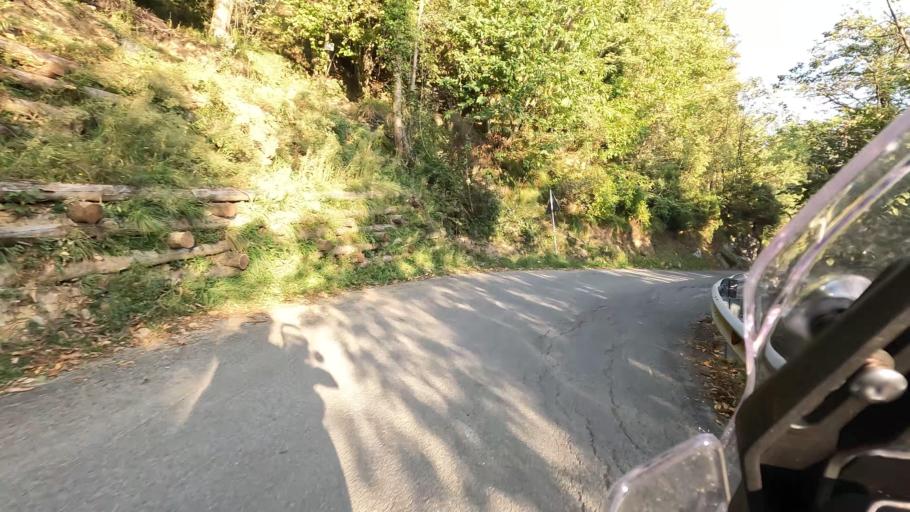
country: IT
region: Liguria
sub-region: Provincia di Savona
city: San Giovanni
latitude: 44.4061
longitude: 8.5255
